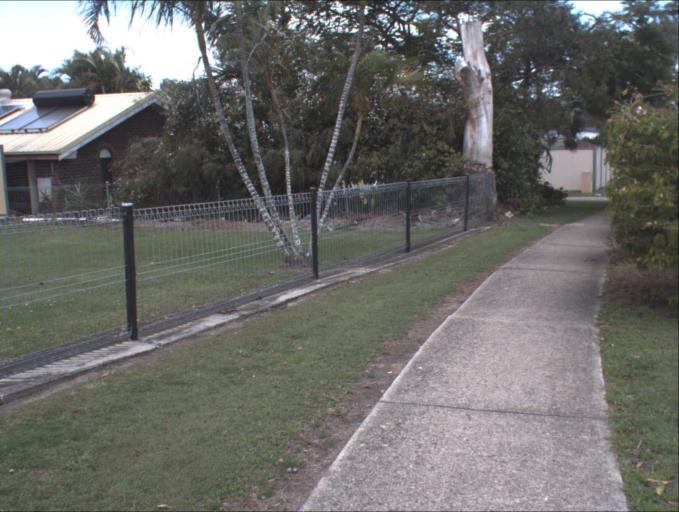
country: AU
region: Queensland
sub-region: Logan
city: Park Ridge South
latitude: -27.6673
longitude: 153.0235
